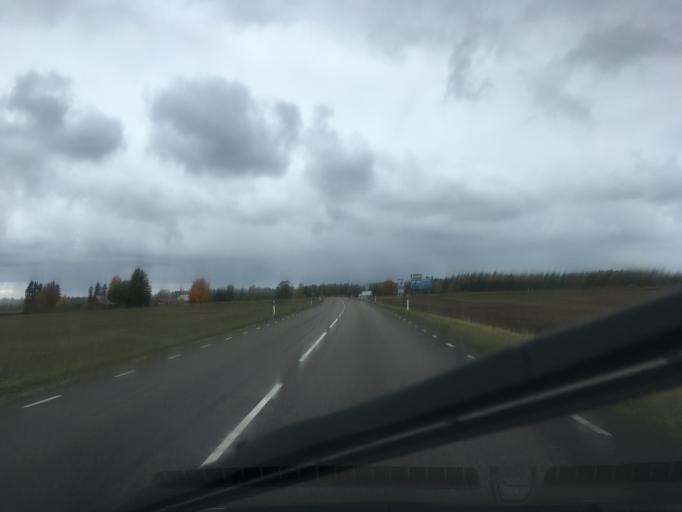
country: EE
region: Harju
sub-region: Anija vald
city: Kehra
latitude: 59.3280
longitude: 25.3241
